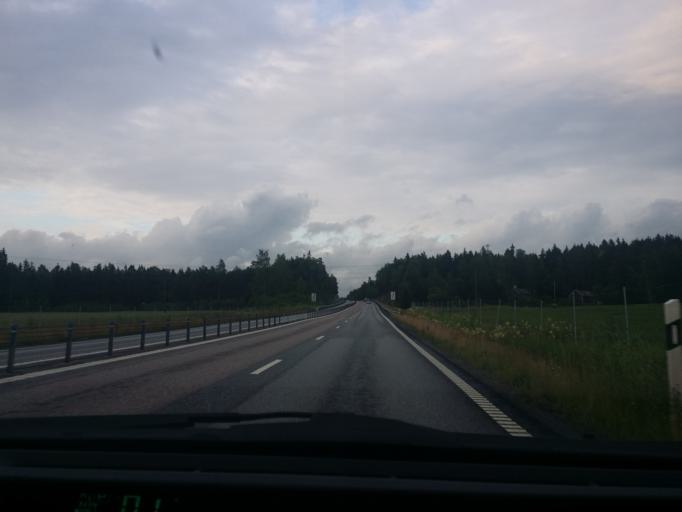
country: SE
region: Vaestmanland
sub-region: Kopings Kommun
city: Koping
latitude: 59.5379
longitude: 15.9974
